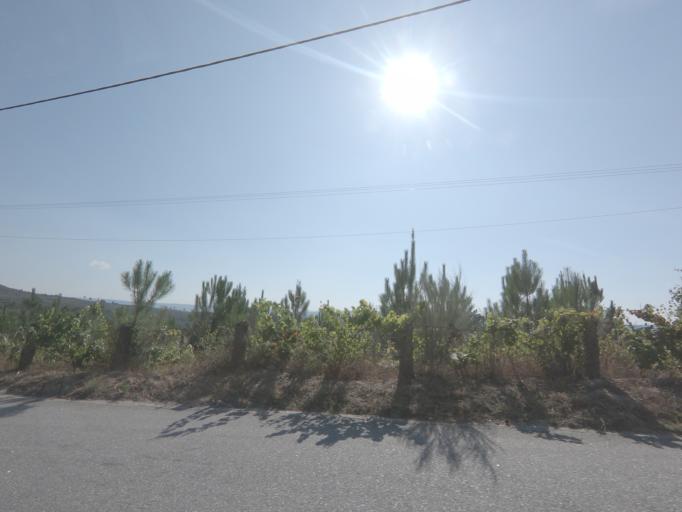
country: PT
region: Viseu
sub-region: Tabuaco
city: Tabuaco
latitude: 41.0429
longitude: -7.5713
